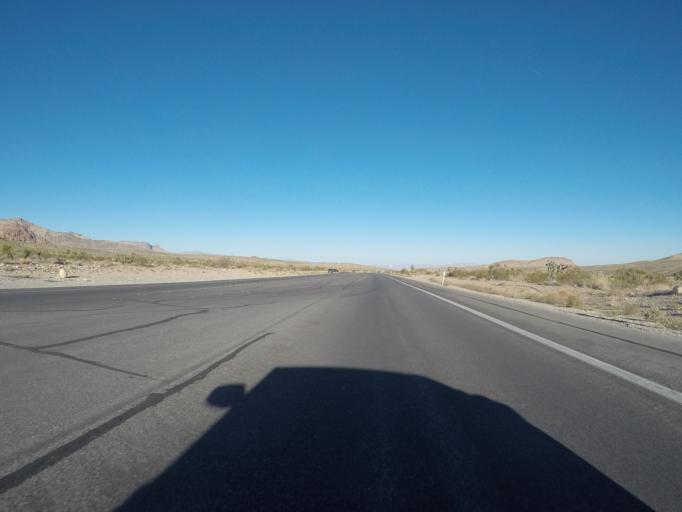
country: US
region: Nevada
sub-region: Clark County
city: Summerlin South
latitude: 36.1303
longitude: -115.4239
